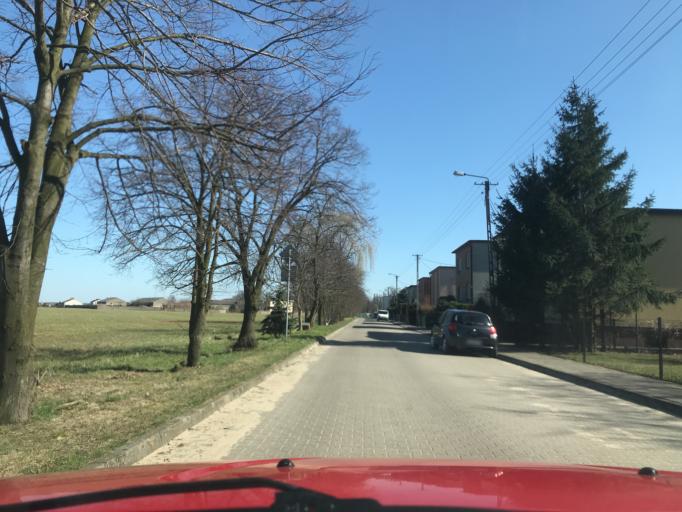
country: PL
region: Greater Poland Voivodeship
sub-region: Powiat jarocinski
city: Witaszyce
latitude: 51.9450
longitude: 17.5541
